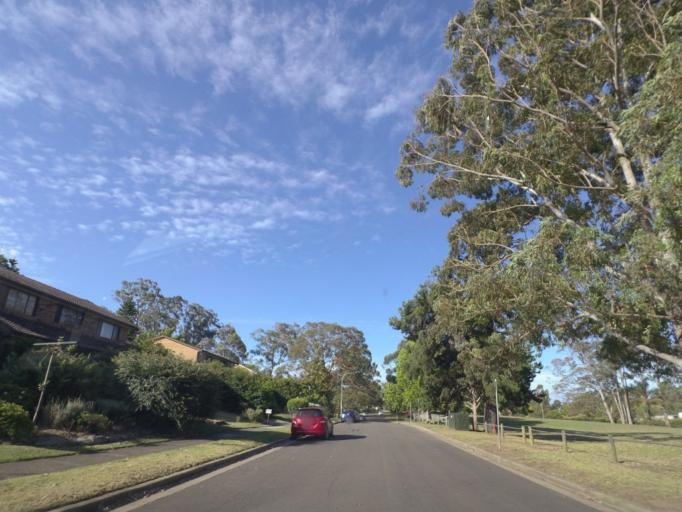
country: AU
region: New South Wales
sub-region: The Hills Shire
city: West Pennant
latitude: -33.7355
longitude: 151.0412
